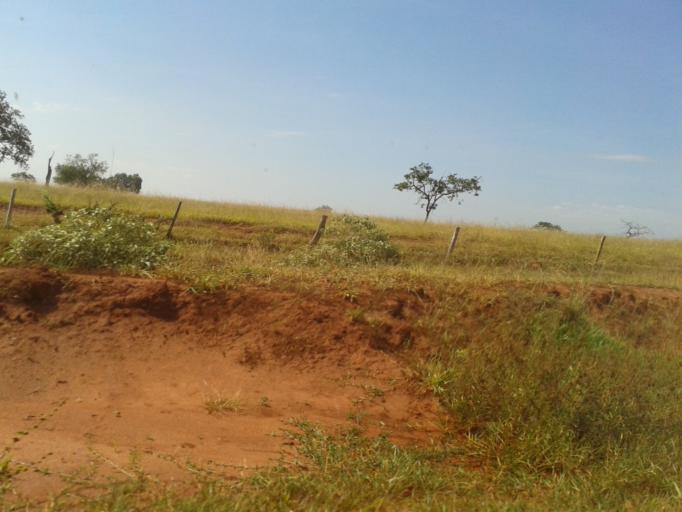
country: BR
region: Minas Gerais
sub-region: Ituiutaba
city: Ituiutaba
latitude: -19.0587
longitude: -49.3642
